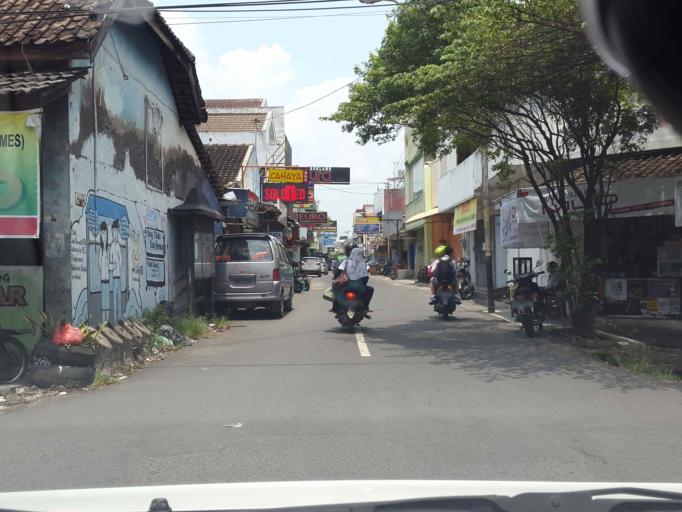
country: ID
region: Central Java
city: Surakarta
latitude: -7.5746
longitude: 110.8206
